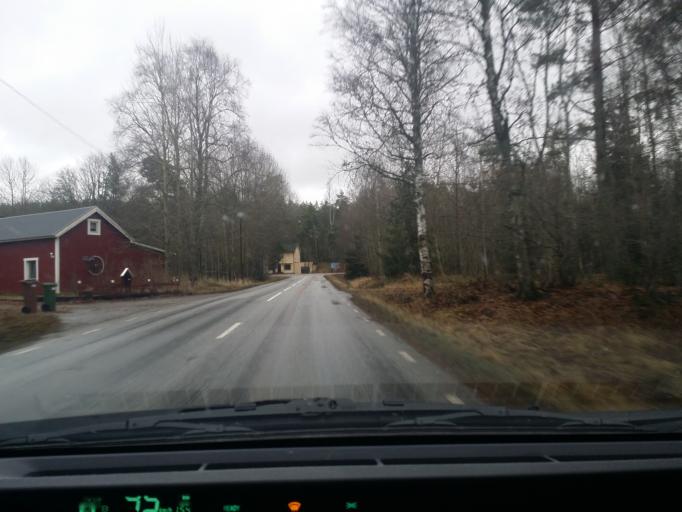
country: SE
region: Vaestmanland
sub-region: Sala Kommun
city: Sala
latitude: 59.8128
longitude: 16.5369
